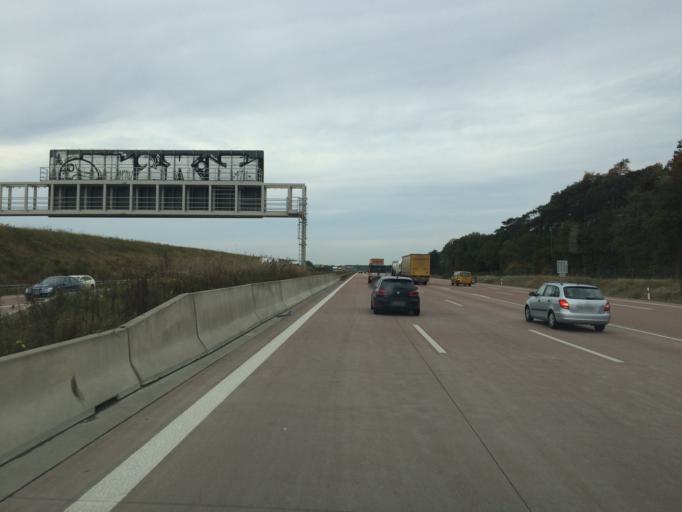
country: DE
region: Brandenburg
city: Michendorf
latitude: 52.3005
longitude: 13.0703
